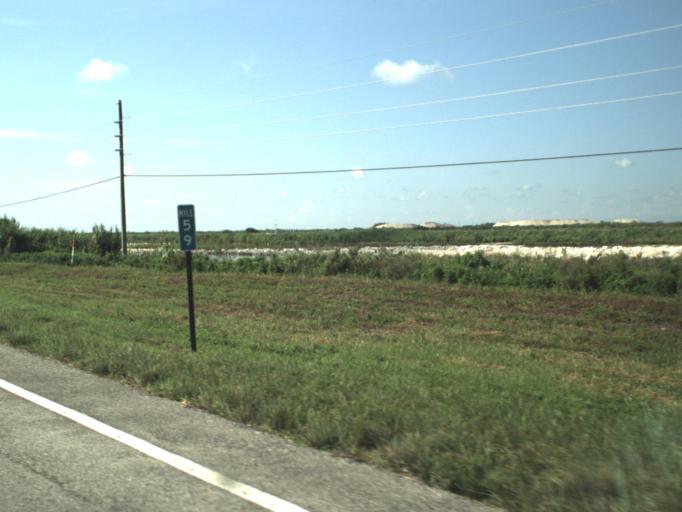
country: US
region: Florida
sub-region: Palm Beach County
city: Belle Glade Camp
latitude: 26.4731
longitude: -80.6451
